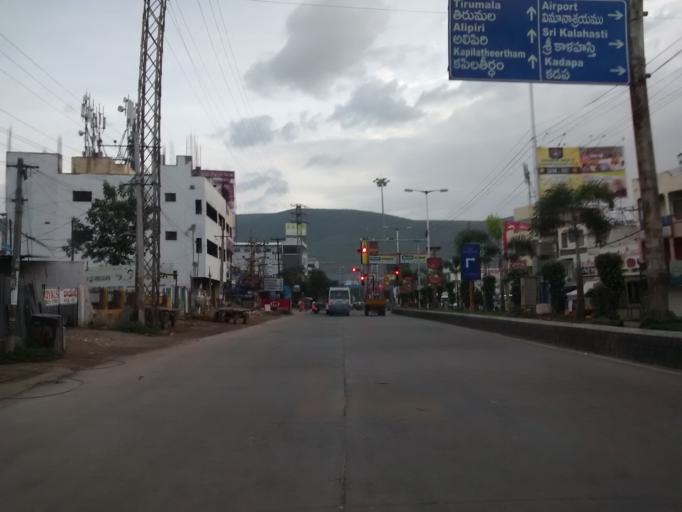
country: IN
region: Andhra Pradesh
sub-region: Chittoor
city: Tirupati
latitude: 13.6410
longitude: 79.4276
